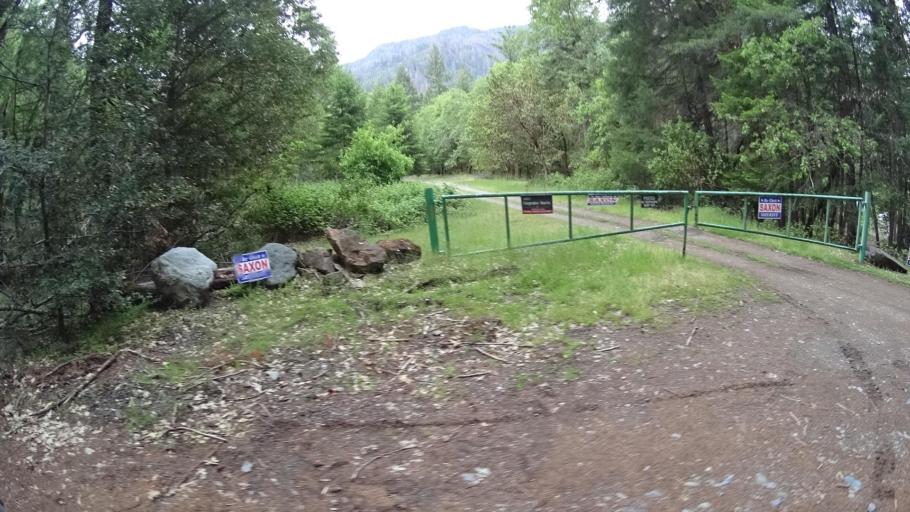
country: US
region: California
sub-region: Humboldt County
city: Willow Creek
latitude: 40.9291
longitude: -123.6155
